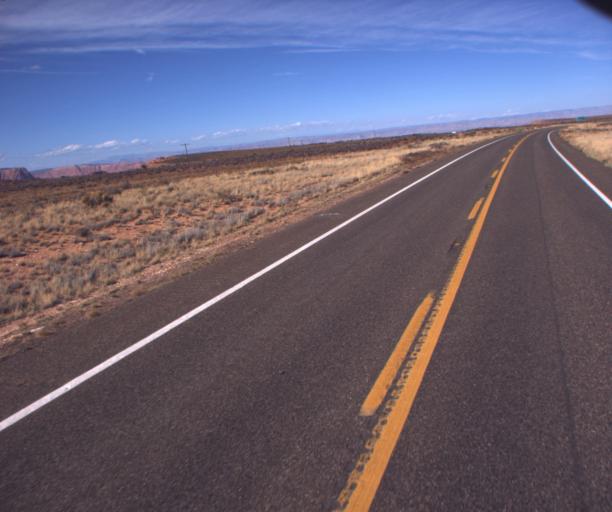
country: US
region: Arizona
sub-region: Coconino County
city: LeChee
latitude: 36.7515
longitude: -111.5742
